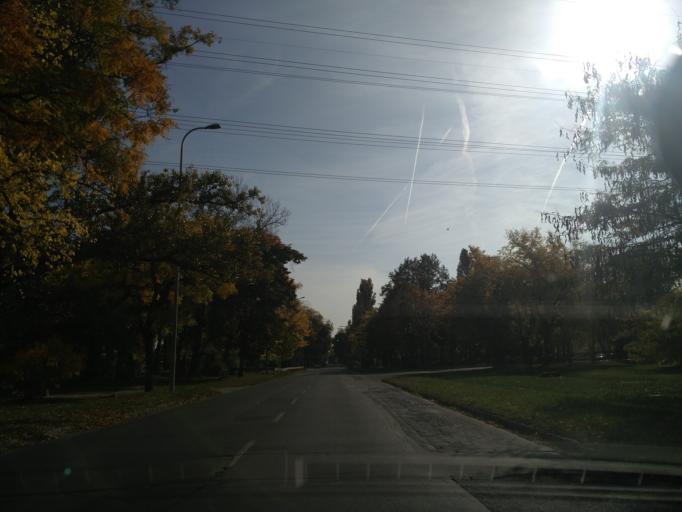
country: HU
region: Budapest
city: Budapest XIV. keruelet
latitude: 47.4794
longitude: 19.1115
